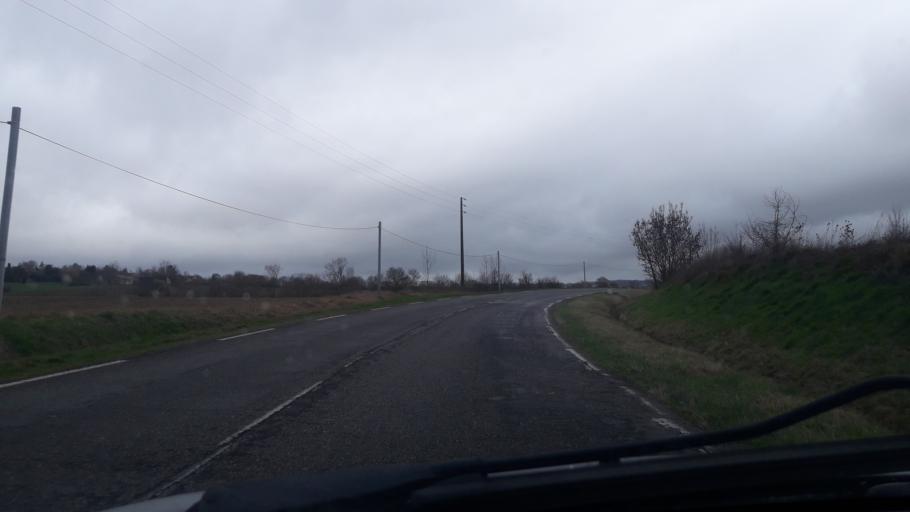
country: FR
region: Midi-Pyrenees
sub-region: Departement du Gers
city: Gimont
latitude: 43.6857
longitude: 1.0007
